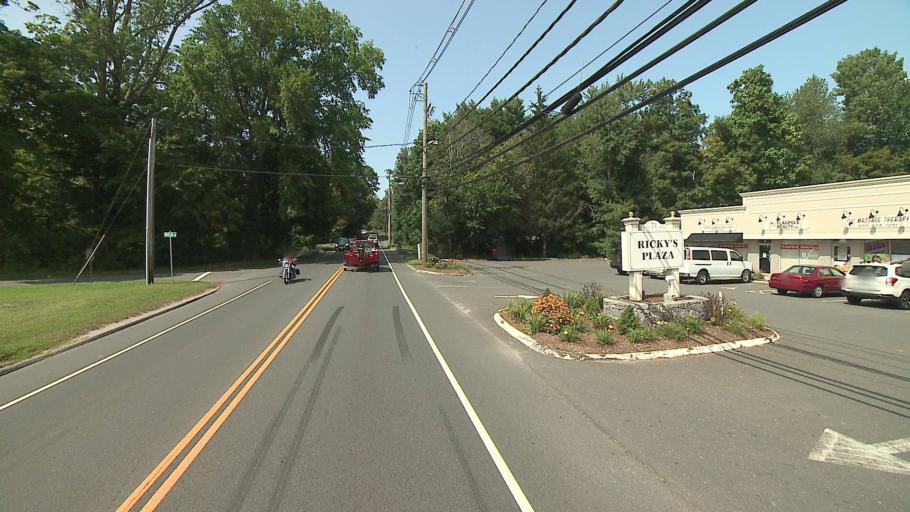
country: US
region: Connecticut
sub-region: Fairfield County
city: Newtown
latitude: 41.3974
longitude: -73.2943
